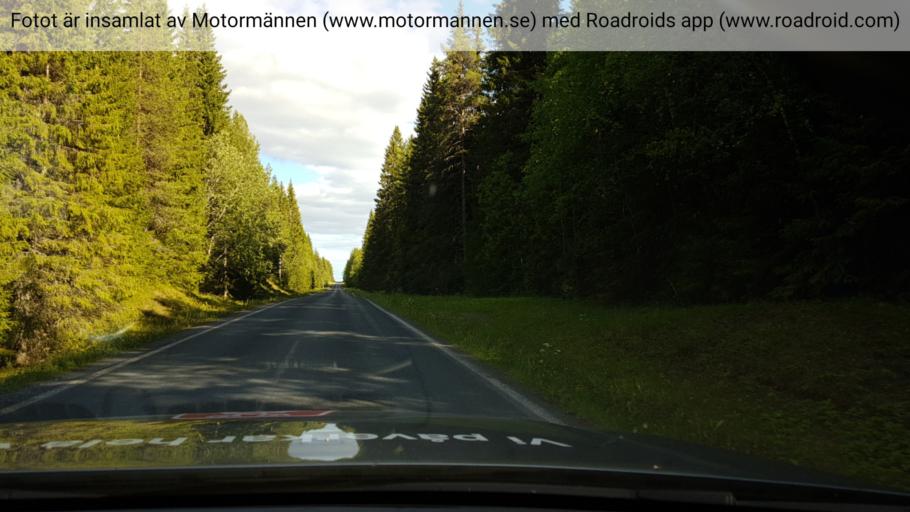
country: SE
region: Jaemtland
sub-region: Krokoms Kommun
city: Valla
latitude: 63.2937
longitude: 13.8541
